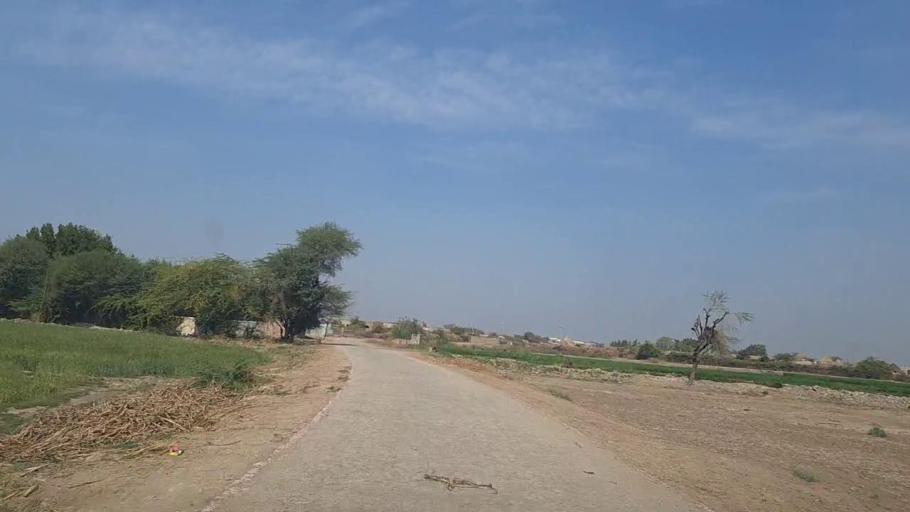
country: PK
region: Sindh
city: Mirpur Khas
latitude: 25.4996
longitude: 68.9210
